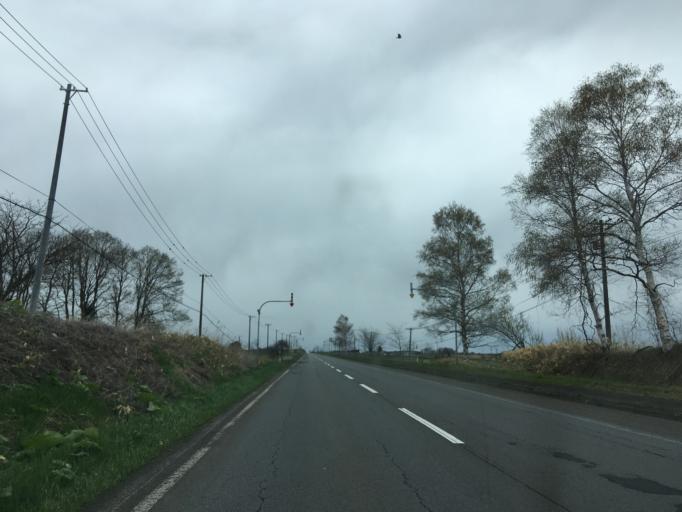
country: JP
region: Hokkaido
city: Chitose
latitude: 42.9191
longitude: 141.8094
